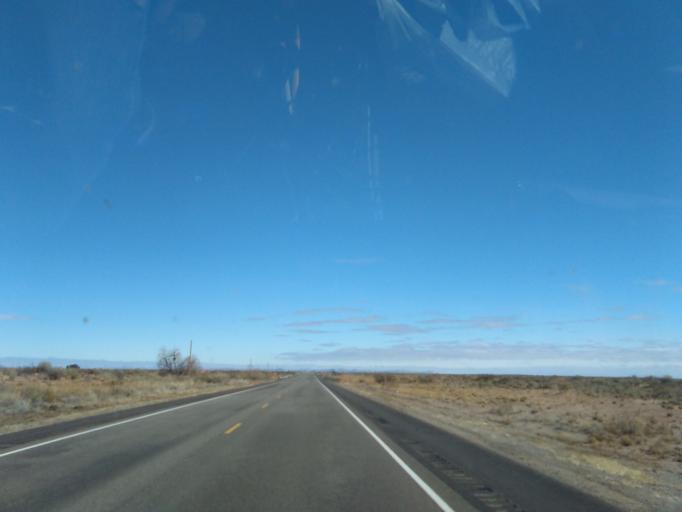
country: US
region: New Mexico
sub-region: Luna County
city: Deming
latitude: 32.2969
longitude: -107.7223
